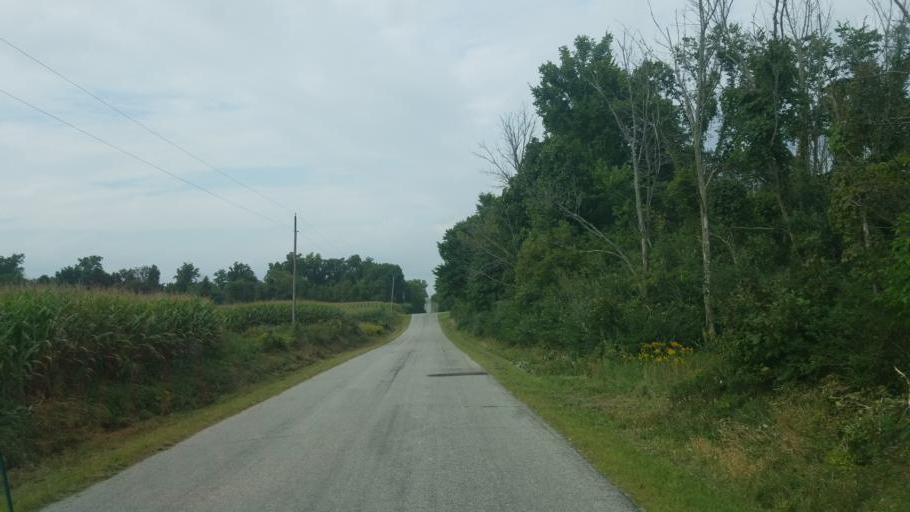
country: US
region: Ohio
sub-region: Wayne County
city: West Salem
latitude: 40.9565
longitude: -82.0536
